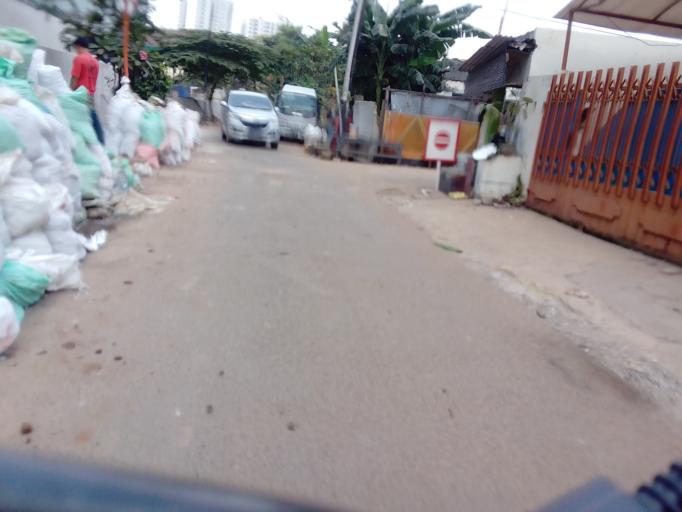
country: ID
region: Jakarta Raya
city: Jakarta
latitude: -6.2041
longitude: 106.8032
